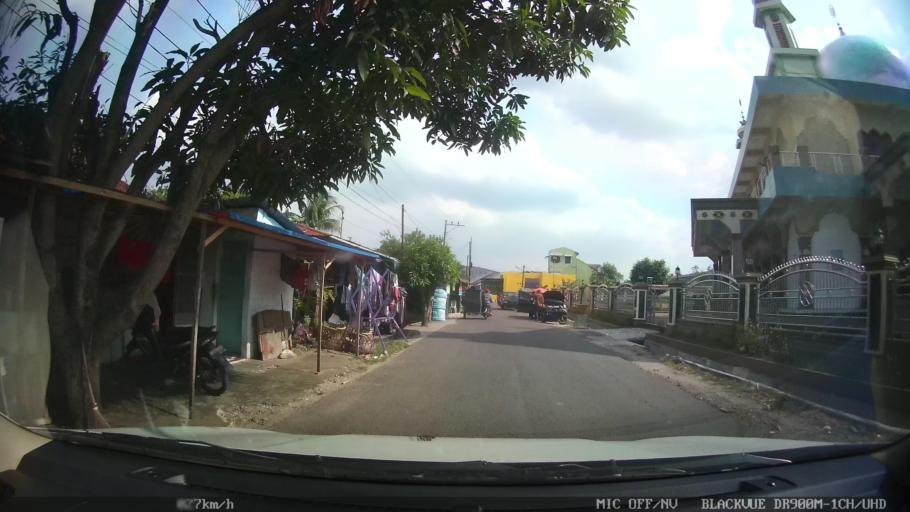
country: ID
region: North Sumatra
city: Binjai
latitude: 3.6100
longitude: 98.5014
